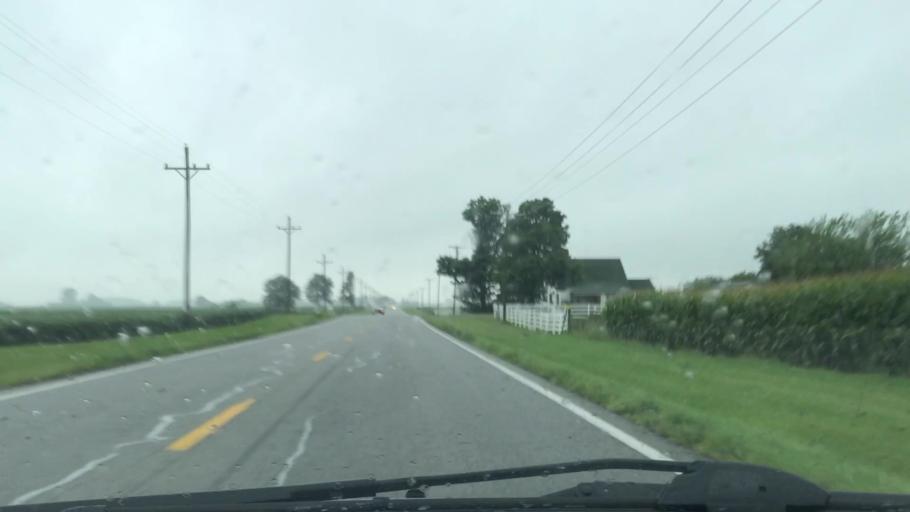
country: US
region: Indiana
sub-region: Hamilton County
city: Sheridan
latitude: 40.1283
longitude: -86.3102
